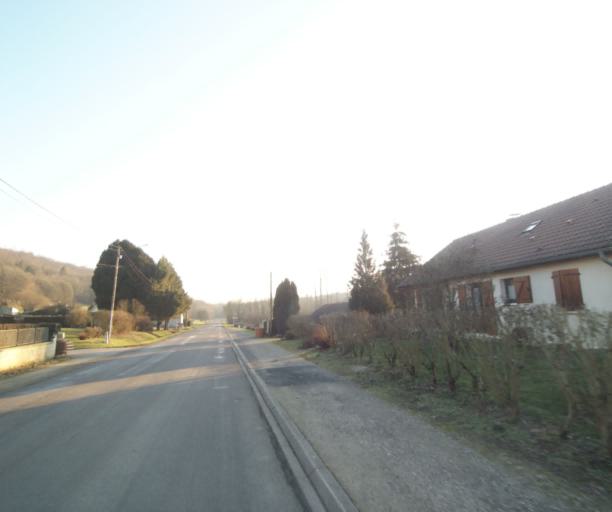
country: FR
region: Champagne-Ardenne
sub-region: Departement de la Haute-Marne
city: Chevillon
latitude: 48.5373
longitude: 5.1060
